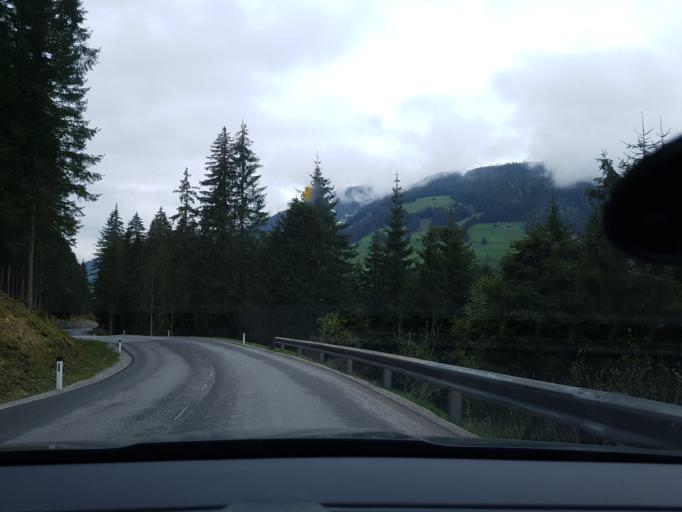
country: AT
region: Tyrol
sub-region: Politischer Bezirk Schwaz
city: Gerlos
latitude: 47.2365
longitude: 12.0642
